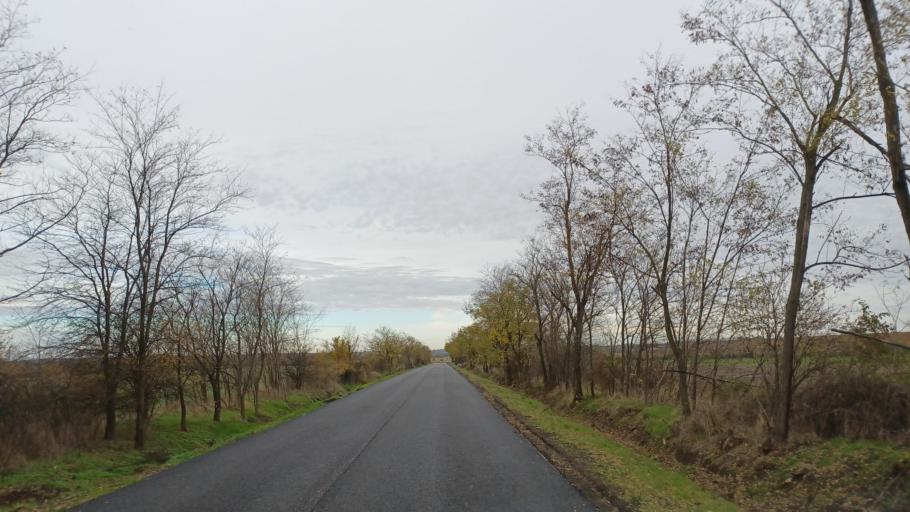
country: HU
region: Tolna
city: Tengelic
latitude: 46.5462
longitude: 18.7525
